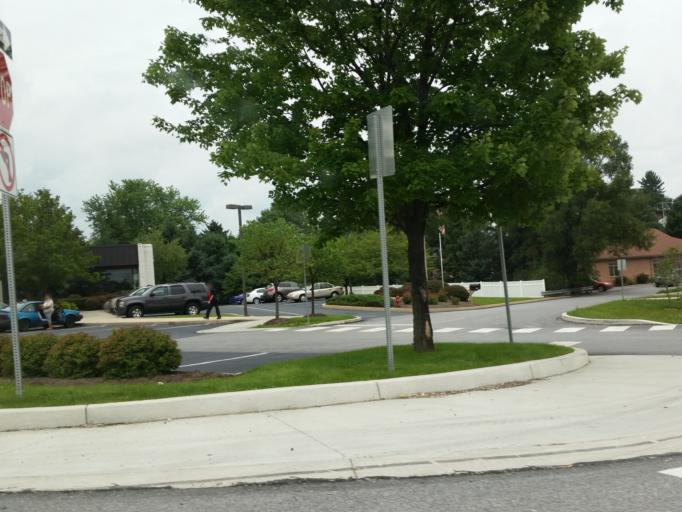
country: US
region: Pennsylvania
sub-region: York County
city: North York
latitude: 39.9843
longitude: -76.7362
